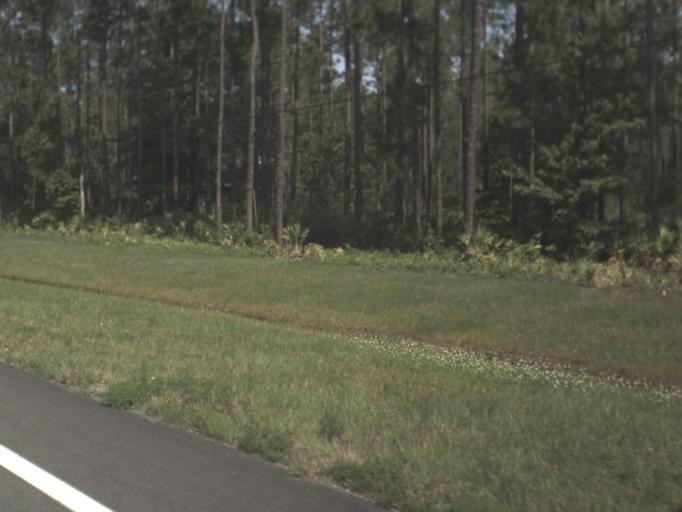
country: US
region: Florida
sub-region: Duval County
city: Baldwin
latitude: 30.2466
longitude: -81.8624
